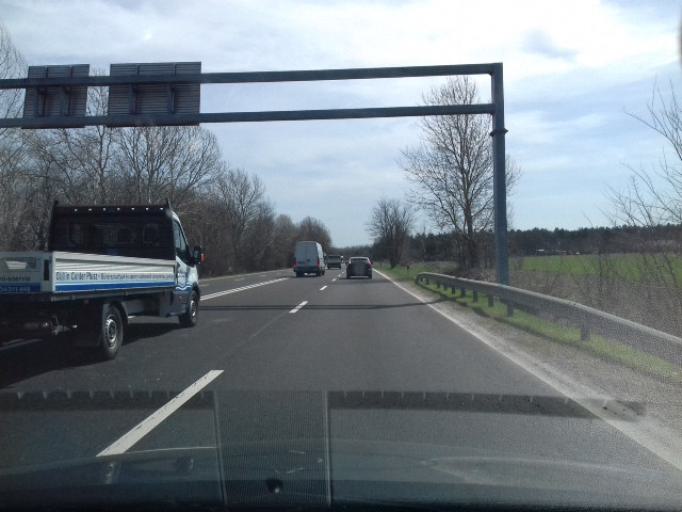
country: HU
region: Bacs-Kiskun
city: Lajosmizse
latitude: 46.9863
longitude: 19.6149
